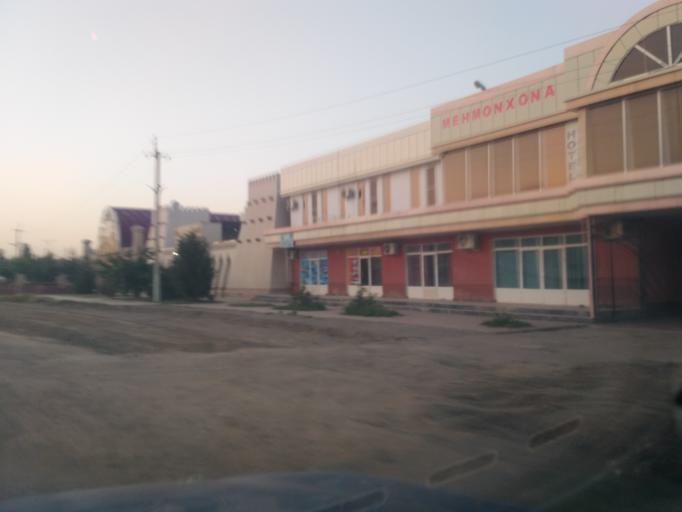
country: UZ
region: Sirdaryo
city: Guliston
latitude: 40.5044
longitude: 68.7685
